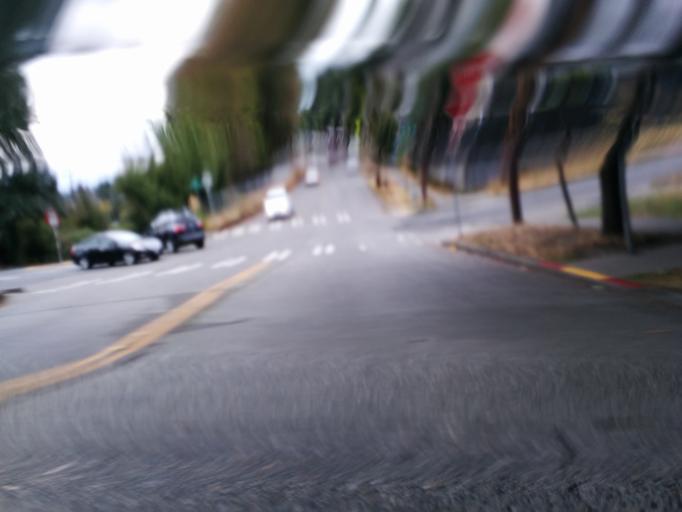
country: US
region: Washington
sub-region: King County
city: Seattle
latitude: 47.6559
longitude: -122.3204
